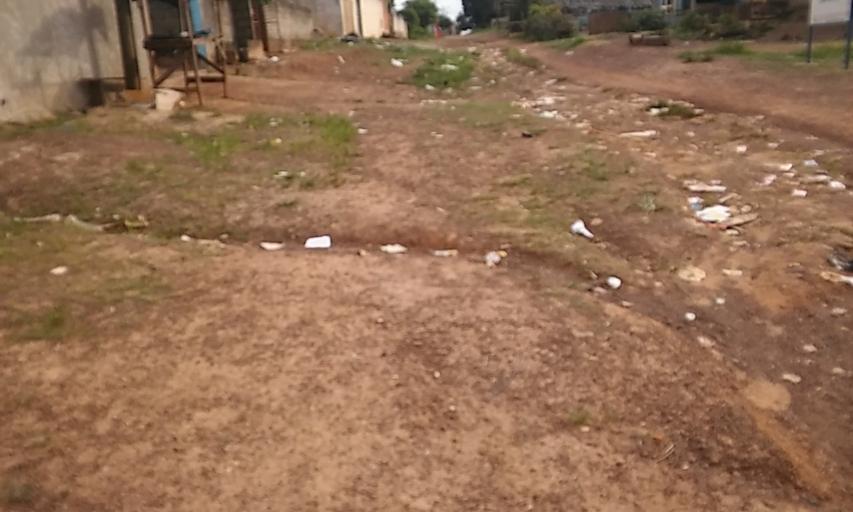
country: CI
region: Dix-Huit Montagnes
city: Duekoue
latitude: 6.7382
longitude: -7.3446
